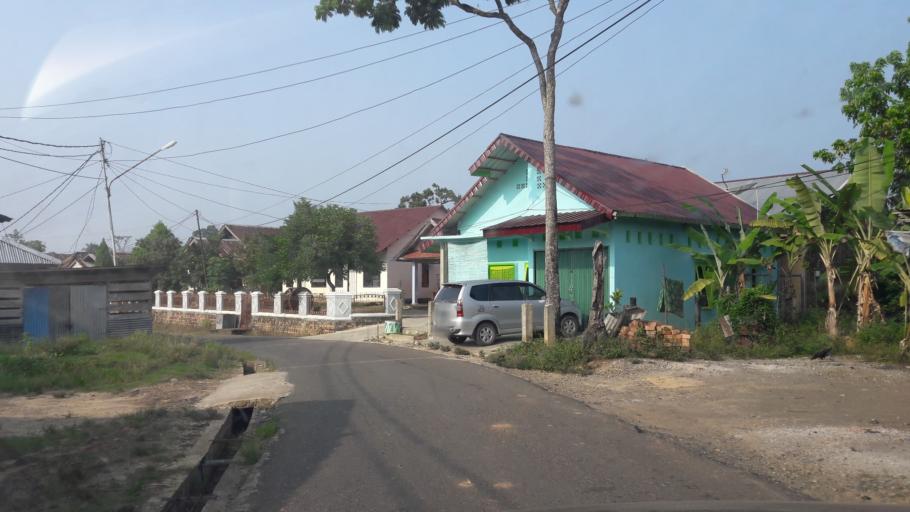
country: ID
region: South Sumatra
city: Gunungmegang Dalam
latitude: -3.2769
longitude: 103.8247
